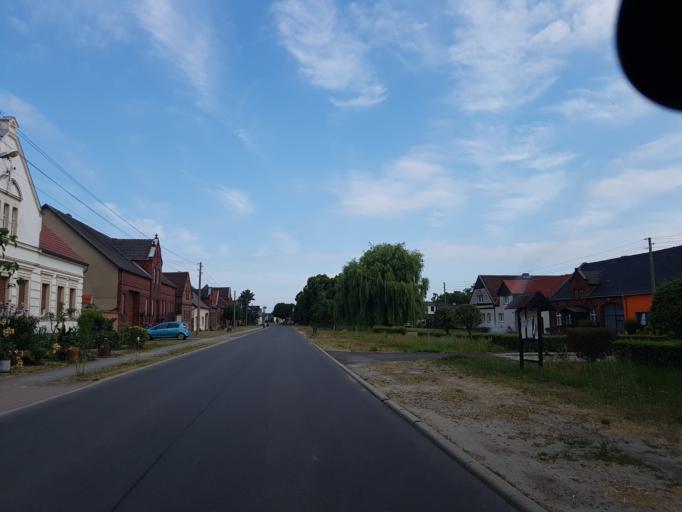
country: DE
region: Brandenburg
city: Luckau
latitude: 51.8378
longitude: 13.6399
